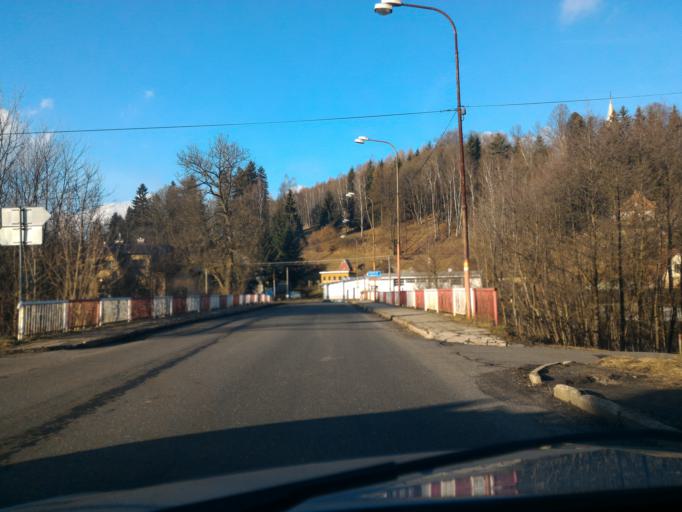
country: CZ
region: Liberecky
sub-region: Okres Jablonec nad Nisou
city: Tanvald
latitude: 50.7365
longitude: 15.2771
